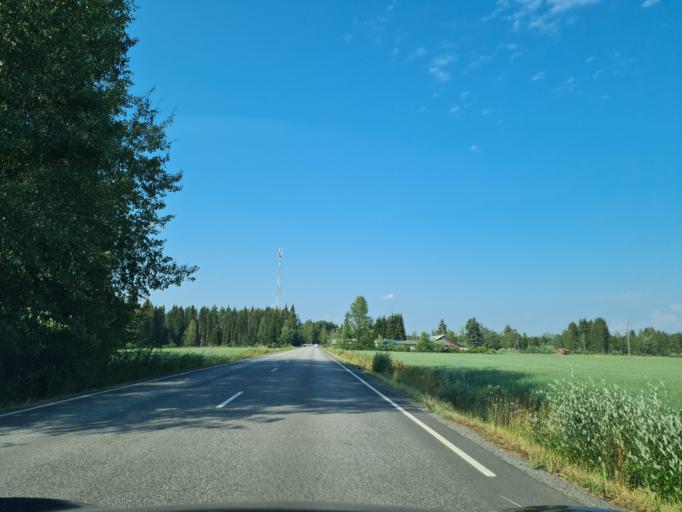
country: FI
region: Satakunta
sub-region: Pohjois-Satakunta
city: Kankaanpaeae
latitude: 61.9396
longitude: 22.5096
